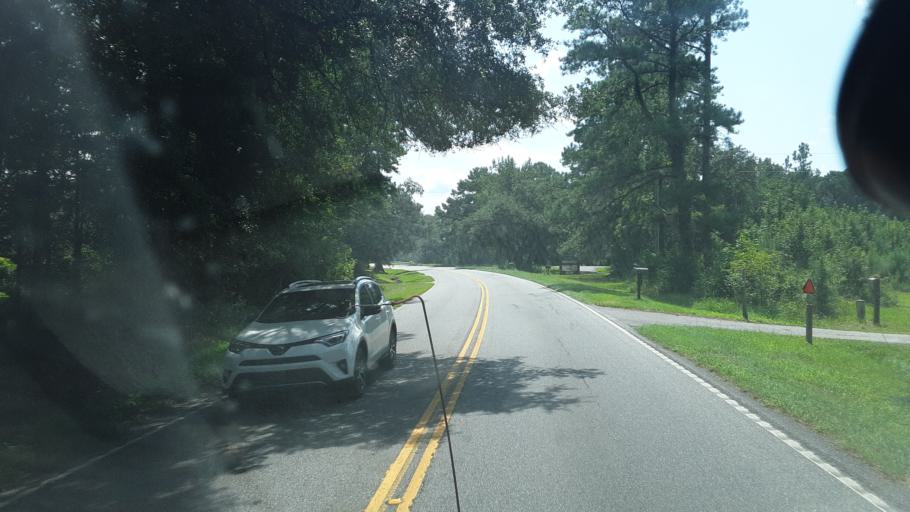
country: US
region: South Carolina
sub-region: Jasper County
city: Ridgeland
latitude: 32.4565
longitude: -80.8989
